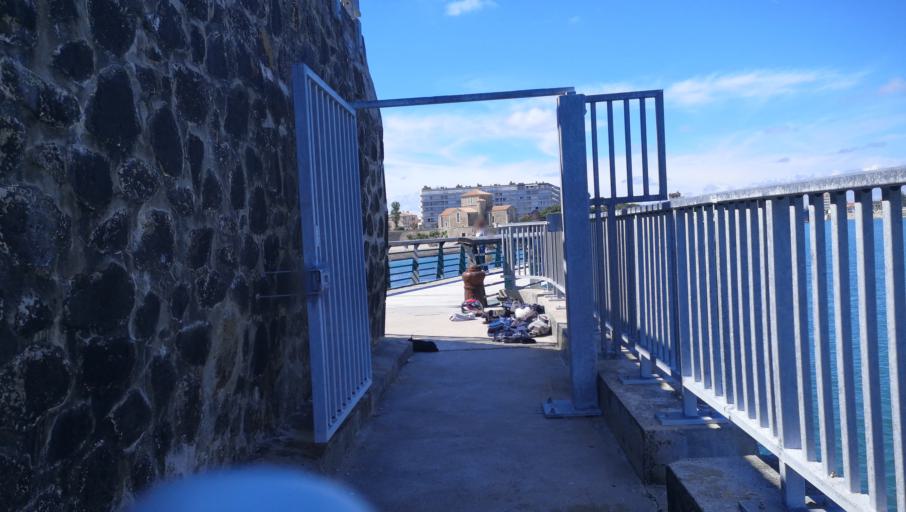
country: FR
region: Pays de la Loire
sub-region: Departement de la Vendee
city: Les Sables-d'Olonne
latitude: 46.4880
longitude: -1.7927
